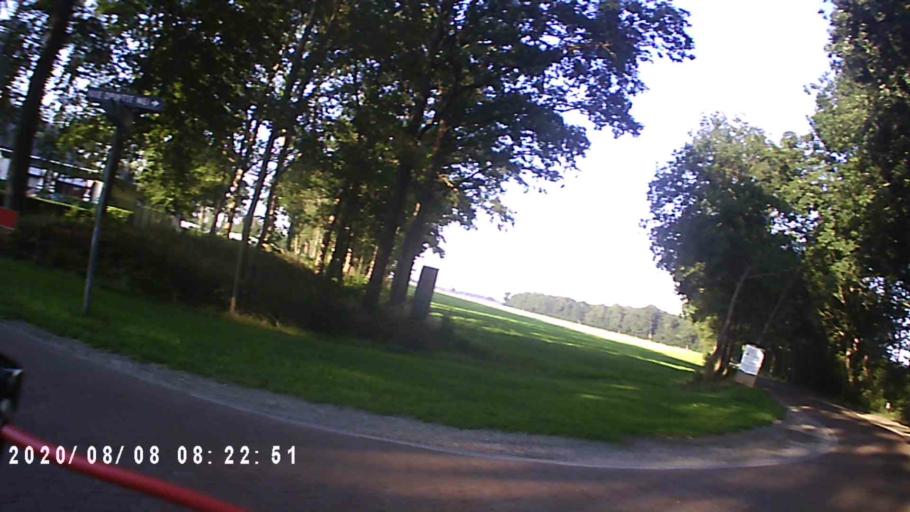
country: NL
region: Groningen
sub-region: Gemeente Leek
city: Leek
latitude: 53.0891
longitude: 6.3112
